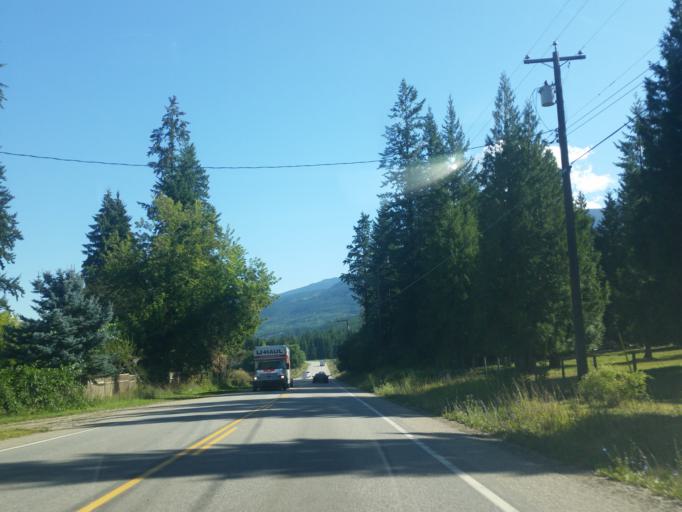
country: CA
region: British Columbia
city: Enderby
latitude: 50.6714
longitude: -119.0611
